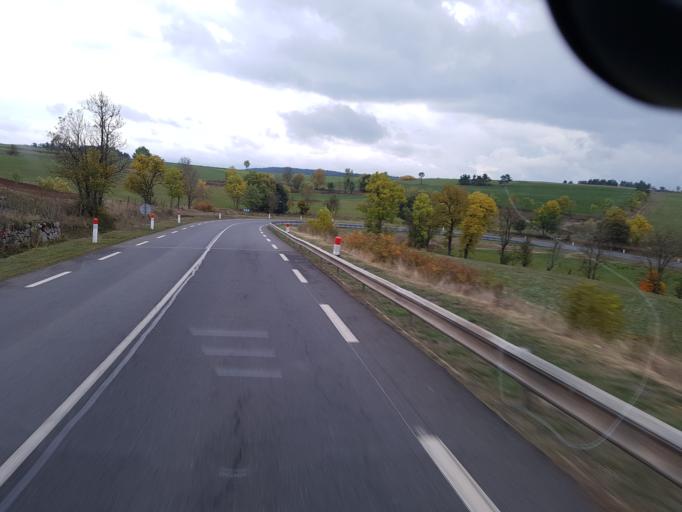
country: FR
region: Languedoc-Roussillon
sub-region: Departement de la Lozere
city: Mende
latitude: 44.5843
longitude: 3.6454
